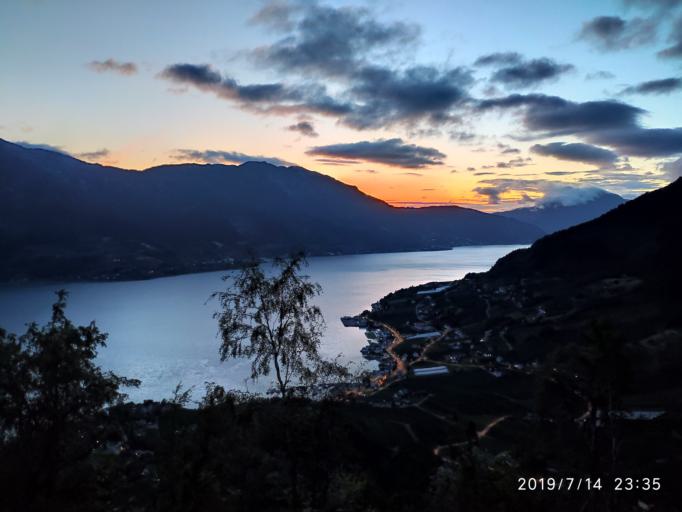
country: NO
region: Hordaland
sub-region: Ullensvang
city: Kinsarvik
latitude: 60.3154
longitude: 6.6642
